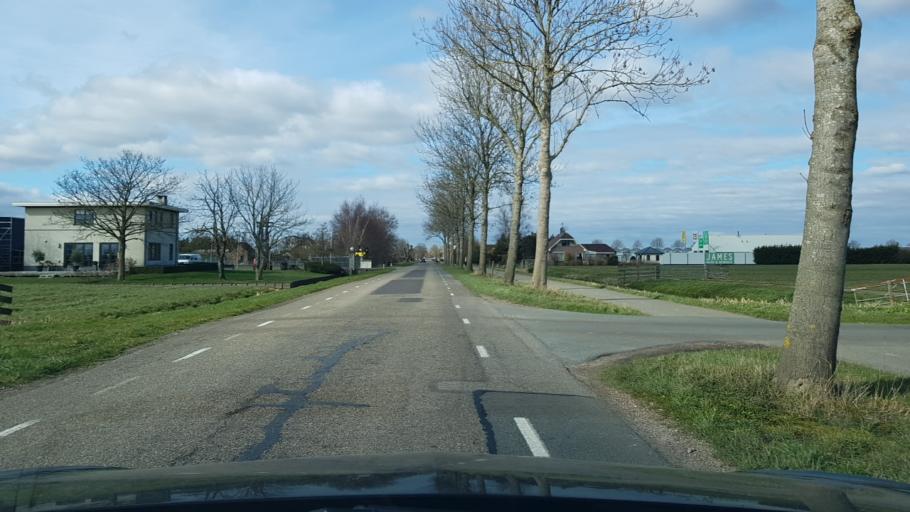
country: NL
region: Utrecht
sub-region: Gemeente De Ronde Venen
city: Mijdrecht
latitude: 52.2041
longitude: 4.8446
